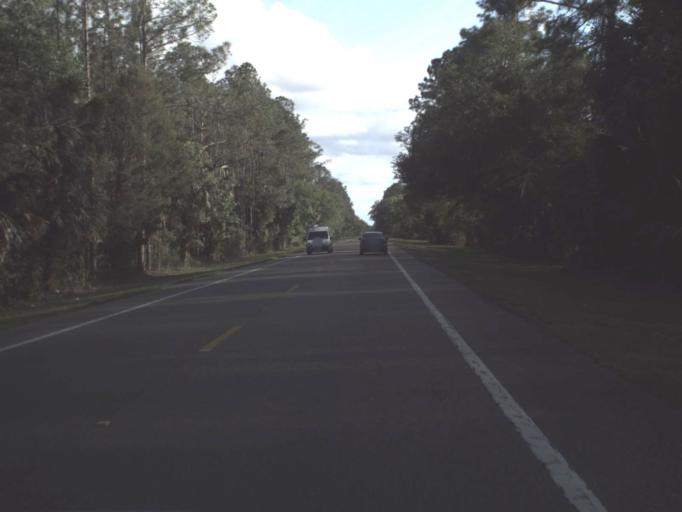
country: US
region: Florida
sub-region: Flagler County
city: Bunnell
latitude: 29.3933
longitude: -81.3081
